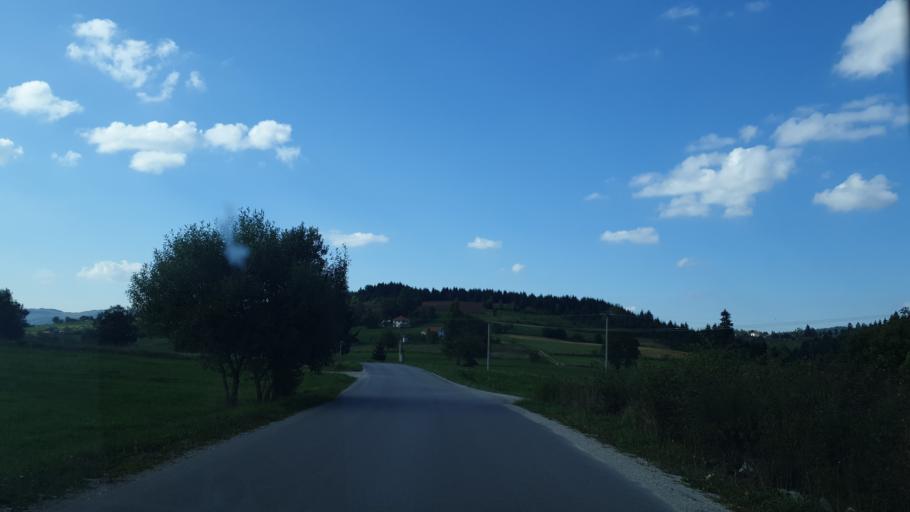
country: RS
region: Central Serbia
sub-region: Zlatiborski Okrug
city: Nova Varos
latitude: 43.4351
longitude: 19.8729
